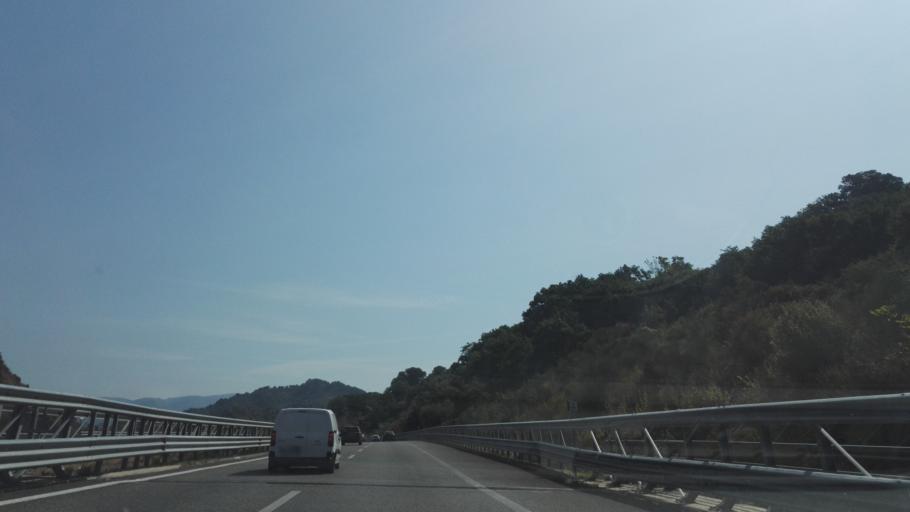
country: IT
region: Calabria
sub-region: Provincia di Catanzaro
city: Martirano Lombardo
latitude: 39.0804
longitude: 16.2096
